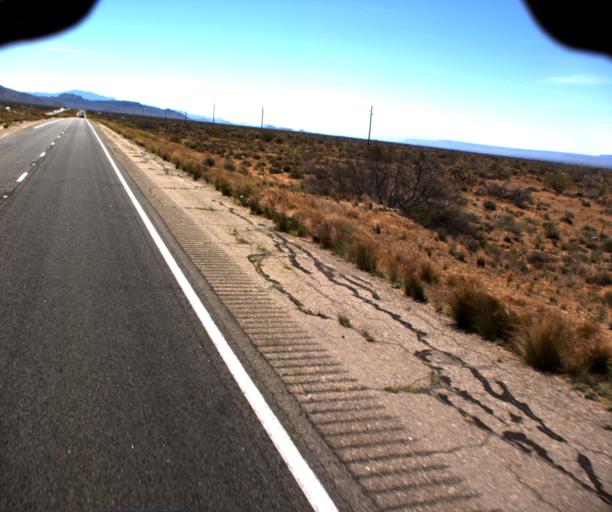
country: US
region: Arizona
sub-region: Mohave County
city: Golden Valley
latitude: 35.3111
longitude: -114.1975
